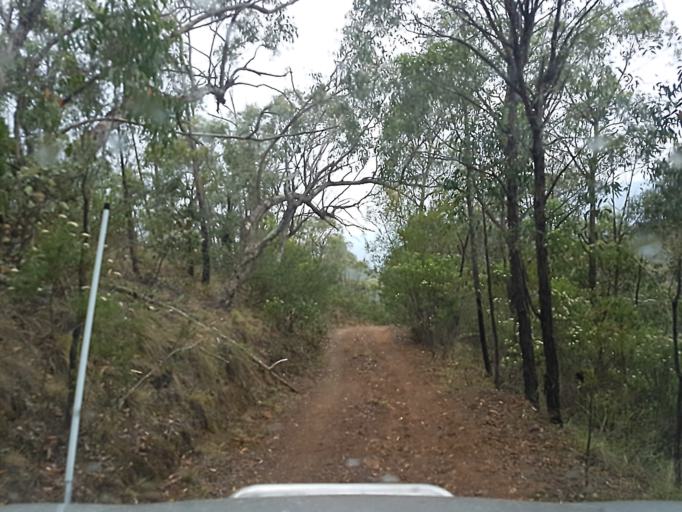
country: AU
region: New South Wales
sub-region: Snowy River
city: Jindabyne
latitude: -36.9228
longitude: 148.3429
